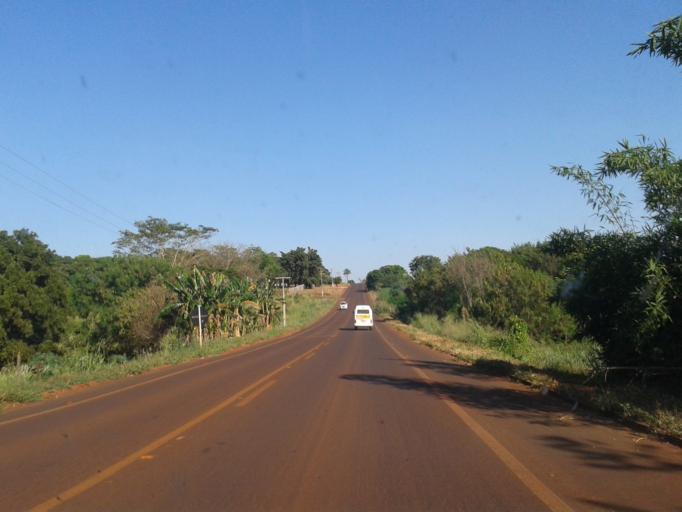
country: BR
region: Minas Gerais
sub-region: Capinopolis
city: Capinopolis
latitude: -18.6846
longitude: -49.5867
